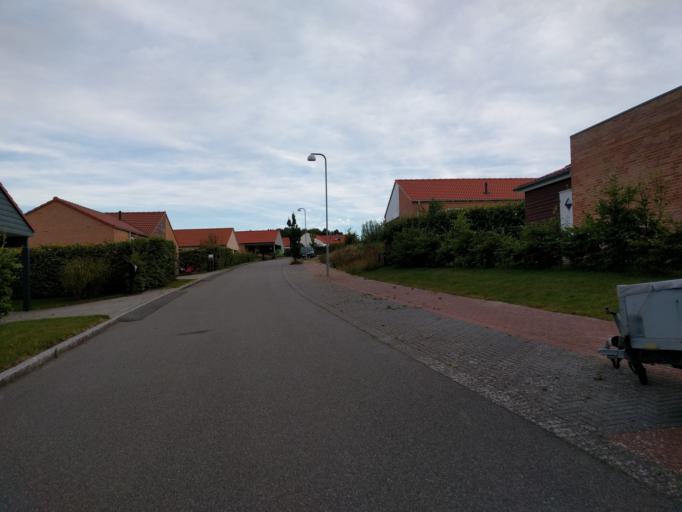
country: DK
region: South Denmark
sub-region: Kerteminde Kommune
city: Munkebo
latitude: 55.4657
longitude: 10.5680
